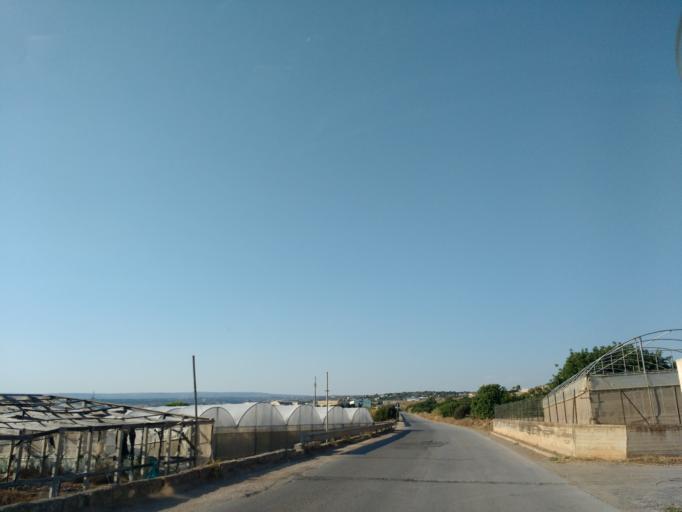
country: IT
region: Sicily
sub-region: Ragusa
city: Cava d'Aliga
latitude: 36.7387
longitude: 14.6824
